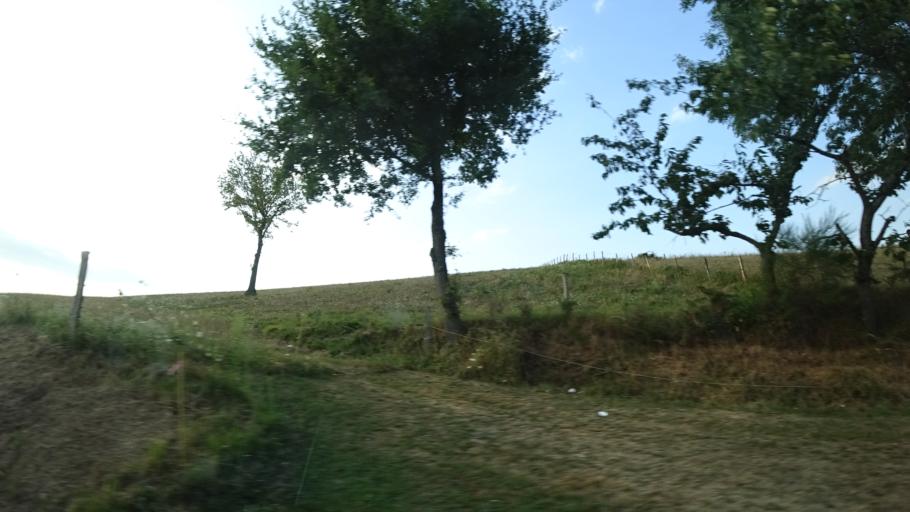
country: FR
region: Midi-Pyrenees
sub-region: Departement de l'Aveyron
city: Livinhac-le-Haut
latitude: 44.6014
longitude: 2.2574
